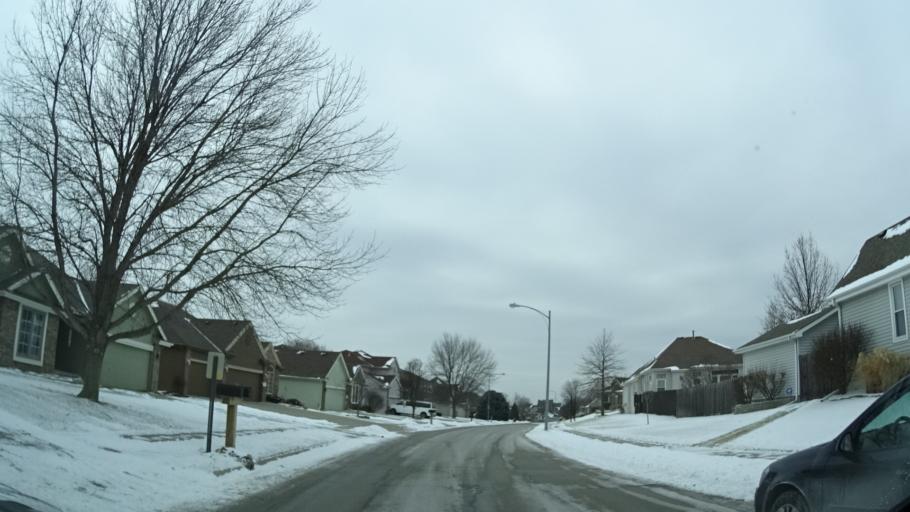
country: US
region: Nebraska
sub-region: Sarpy County
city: Offutt Air Force Base
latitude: 41.1633
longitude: -95.9497
